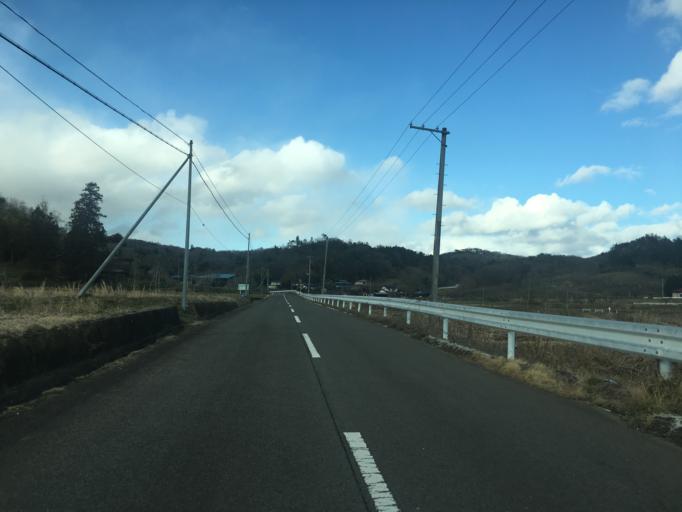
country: JP
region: Fukushima
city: Yanagawamachi-saiwaicho
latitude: 37.8826
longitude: 140.5998
